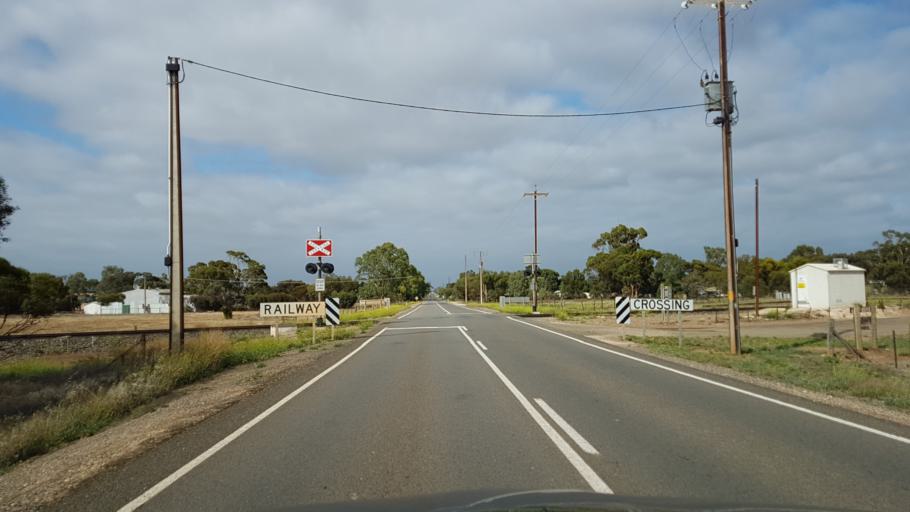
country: AU
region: South Australia
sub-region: Mount Barker
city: Callington
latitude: -35.1110
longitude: 139.0464
